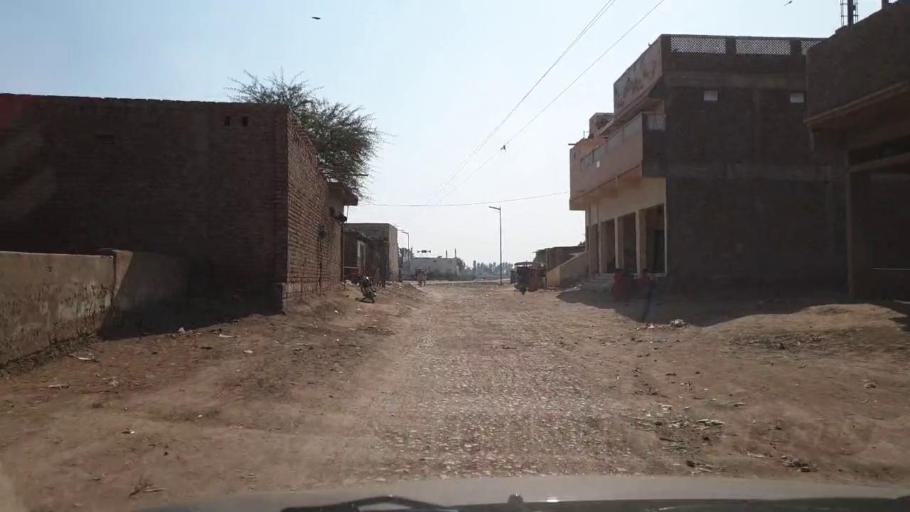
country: PK
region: Sindh
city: Jhol
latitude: 25.9508
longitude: 68.8866
